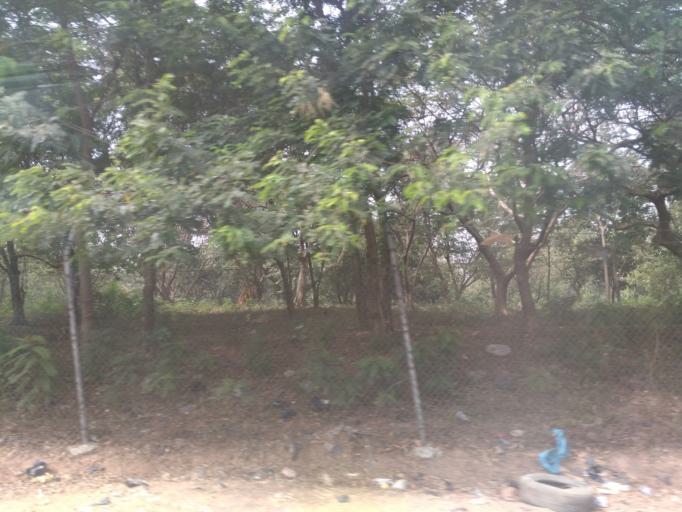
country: GH
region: Ashanti
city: Kumasi
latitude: 6.7049
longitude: -1.6108
